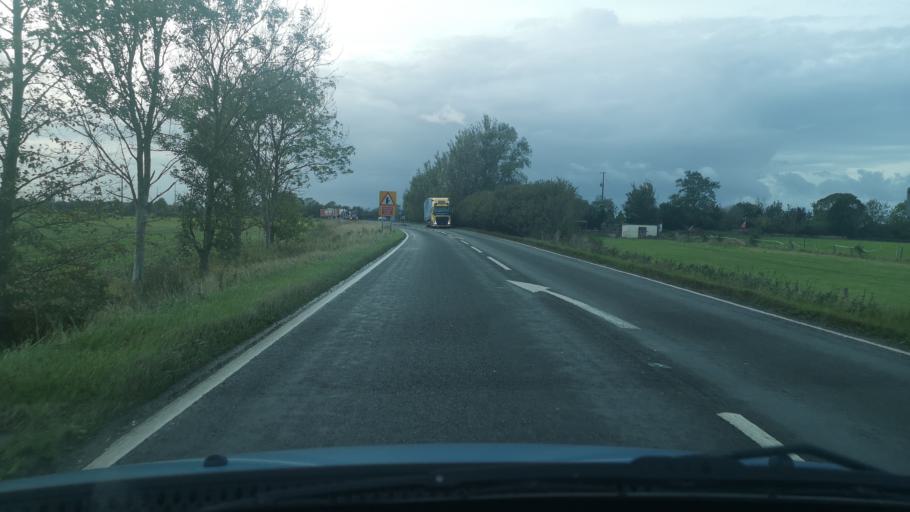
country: GB
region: England
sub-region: Doncaster
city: Hatfield
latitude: 53.5931
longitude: -0.9444
